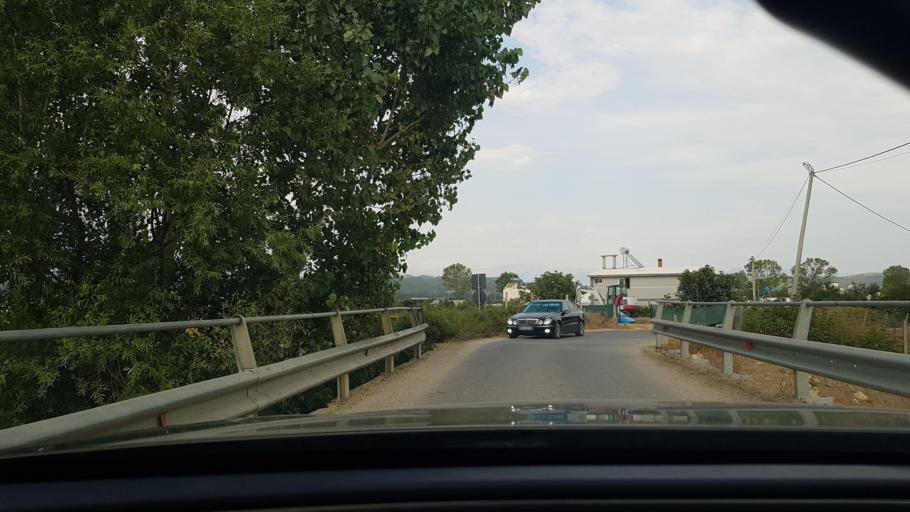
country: AL
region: Durres
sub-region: Rrethi i Durresit
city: Katundi i Ri
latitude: 41.4851
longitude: 19.5260
